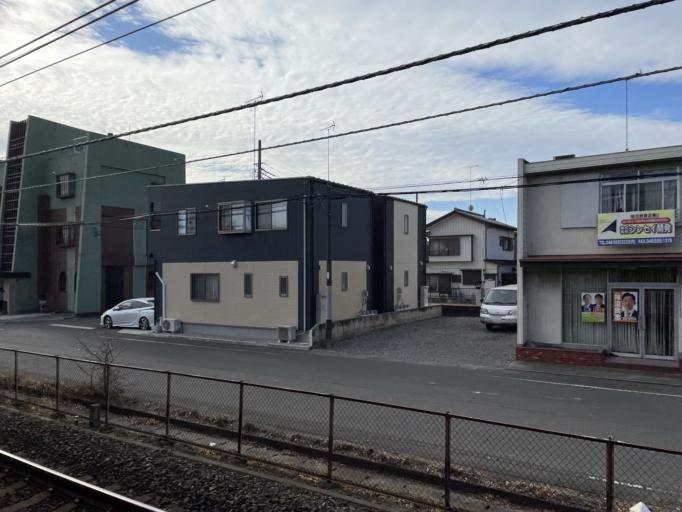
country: JP
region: Saitama
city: Fukiage-fujimi
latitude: 36.1130
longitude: 139.4327
